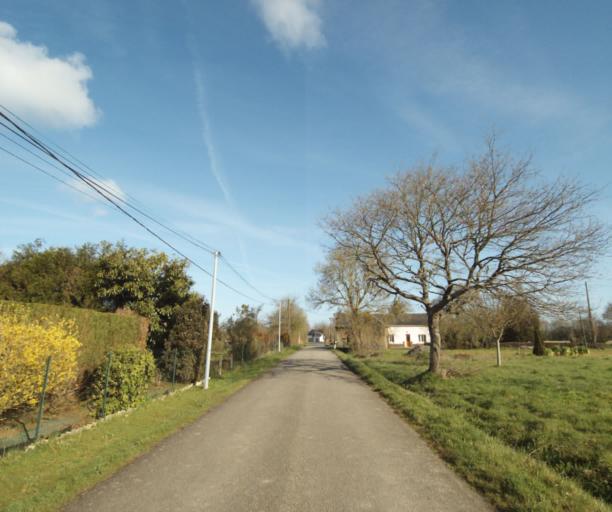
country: FR
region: Pays de la Loire
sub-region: Departement de la Loire-Atlantique
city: Bouvron
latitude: 47.4070
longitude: -1.8401
